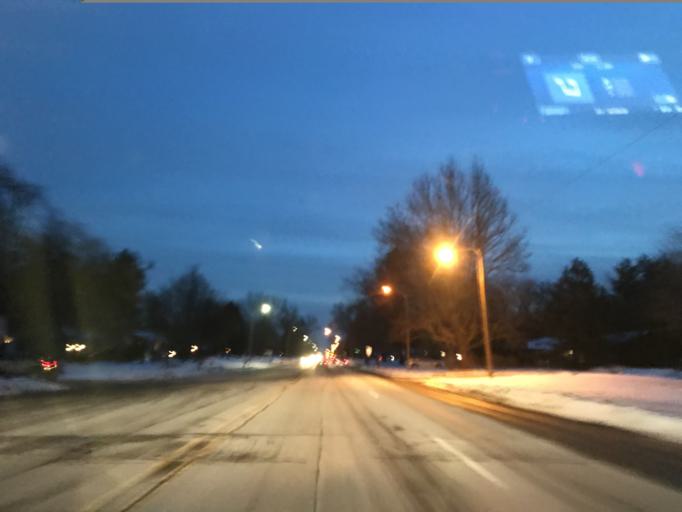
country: US
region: Michigan
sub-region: Wayne County
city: Redford
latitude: 42.4130
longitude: -83.3156
